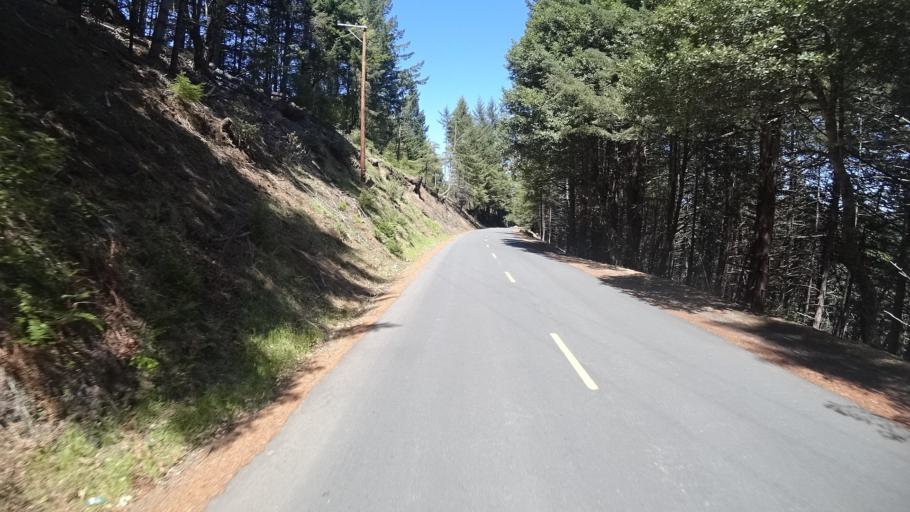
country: US
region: California
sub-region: Humboldt County
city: Rio Dell
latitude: 40.2957
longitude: -124.0573
